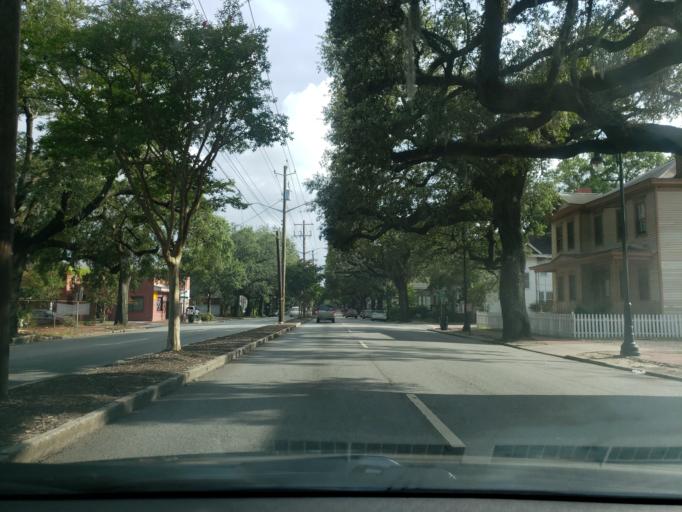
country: US
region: Georgia
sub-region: Chatham County
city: Savannah
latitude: 32.0606
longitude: -81.1047
